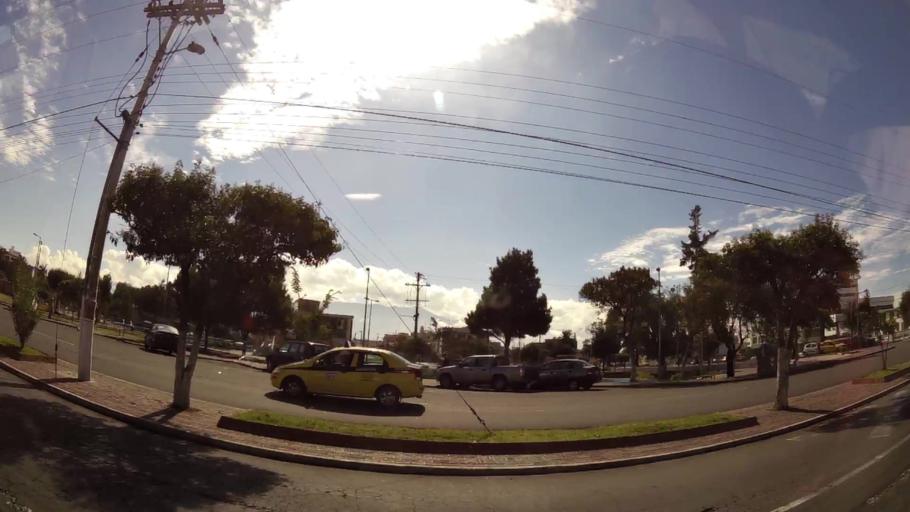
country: EC
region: Chimborazo
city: Riobamba
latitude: -1.6674
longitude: -78.6599
